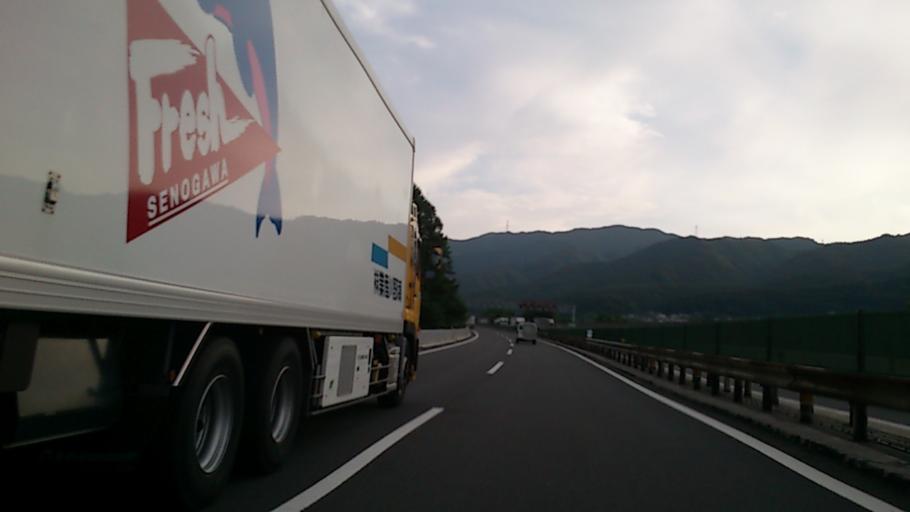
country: JP
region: Nagano
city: Okaya
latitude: 36.0498
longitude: 138.0355
